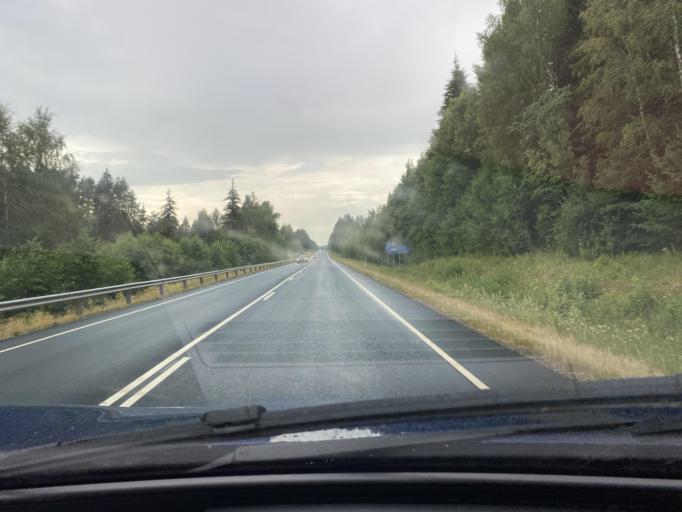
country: FI
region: Central Ostrobothnia
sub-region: Kaustinen
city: Veteli
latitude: 63.4189
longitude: 23.9390
